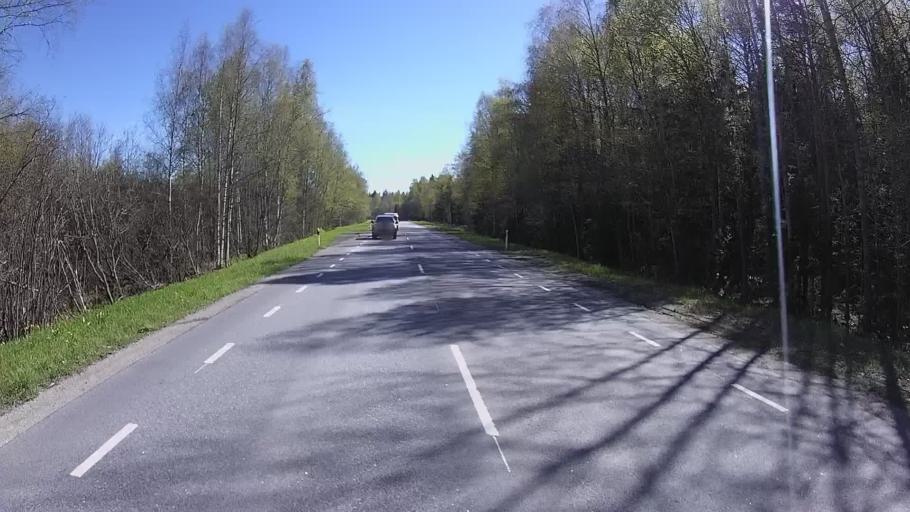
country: EE
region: Harju
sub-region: Loksa linn
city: Loksa
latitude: 59.5626
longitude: 25.7250
